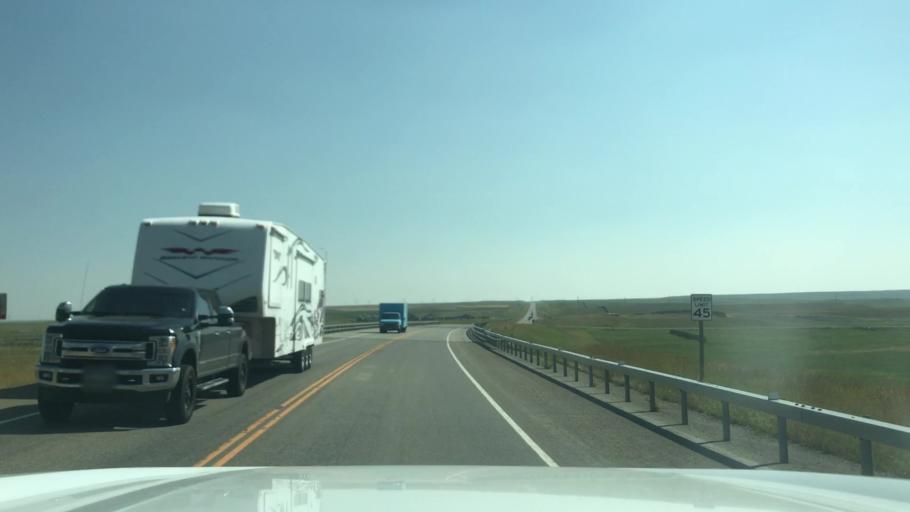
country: US
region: Montana
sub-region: Wheatland County
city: Harlowton
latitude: 46.6748
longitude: -109.7525
